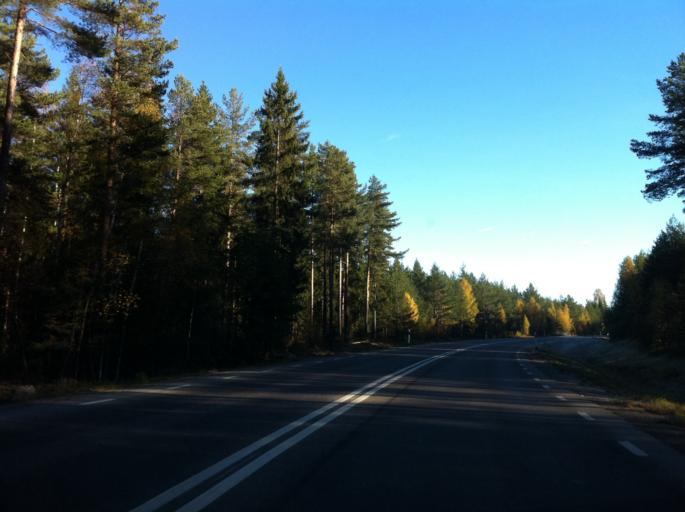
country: SE
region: Gaevleborg
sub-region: Gavle Kommun
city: Gavle
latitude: 60.6334
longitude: 17.1255
